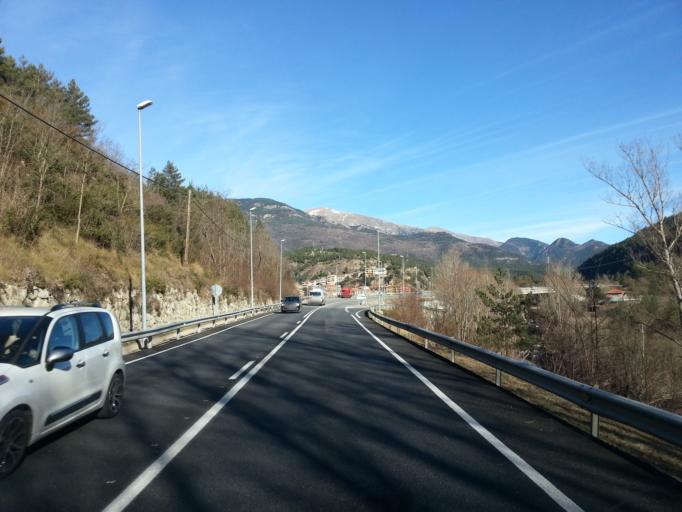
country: ES
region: Catalonia
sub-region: Provincia de Barcelona
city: Guardiola de Bergueda
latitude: 42.2265
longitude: 1.8747
